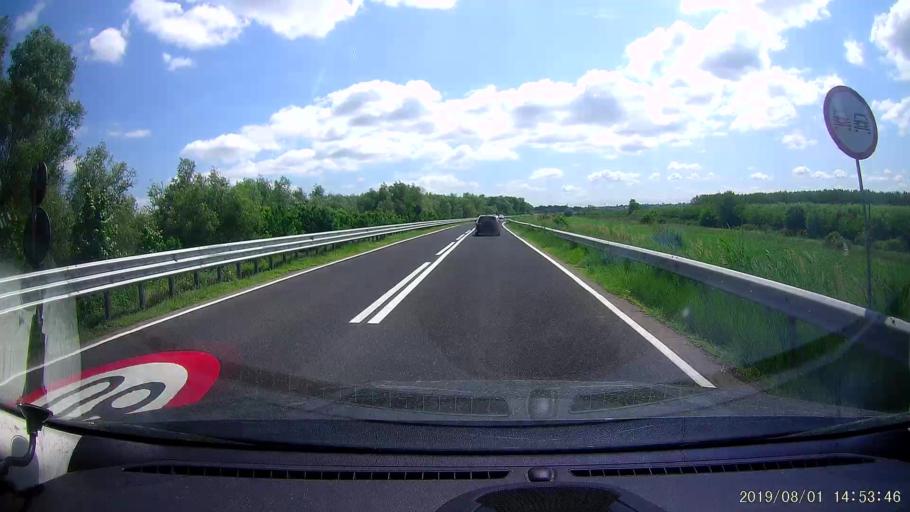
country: RO
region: Braila
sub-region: Municipiul Braila
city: Braila
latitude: 45.3291
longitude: 27.9989
